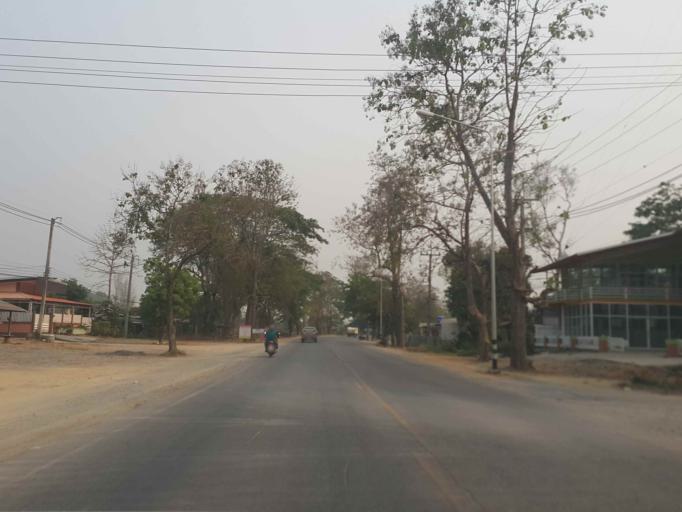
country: TH
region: Chiang Mai
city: Mae Taeng
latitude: 18.9939
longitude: 98.9779
